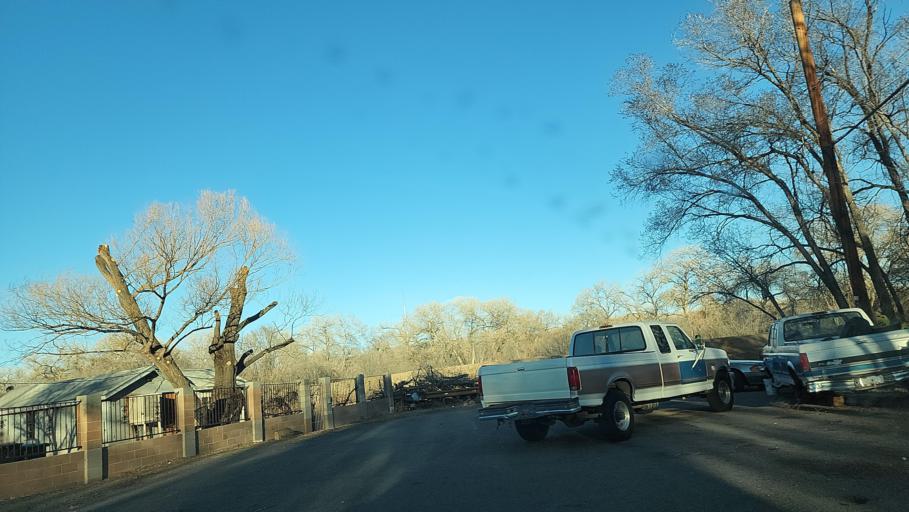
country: US
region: New Mexico
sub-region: Bernalillo County
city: South Valley
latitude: 35.0307
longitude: -106.6747
